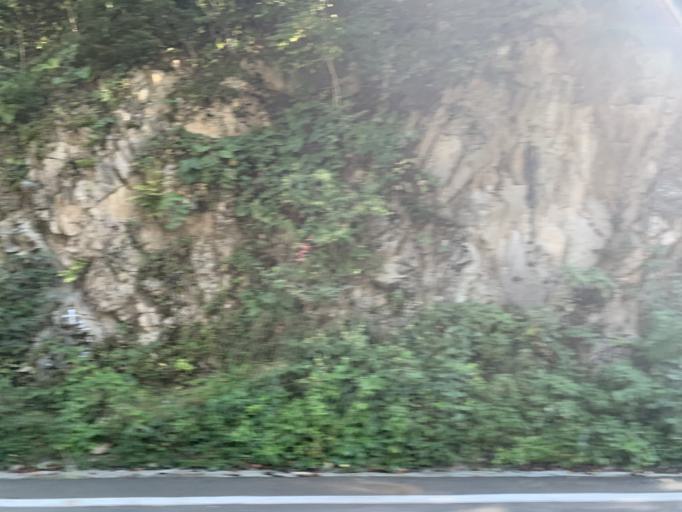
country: TR
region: Trabzon
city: Macka
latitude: 40.7041
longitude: 39.6508
